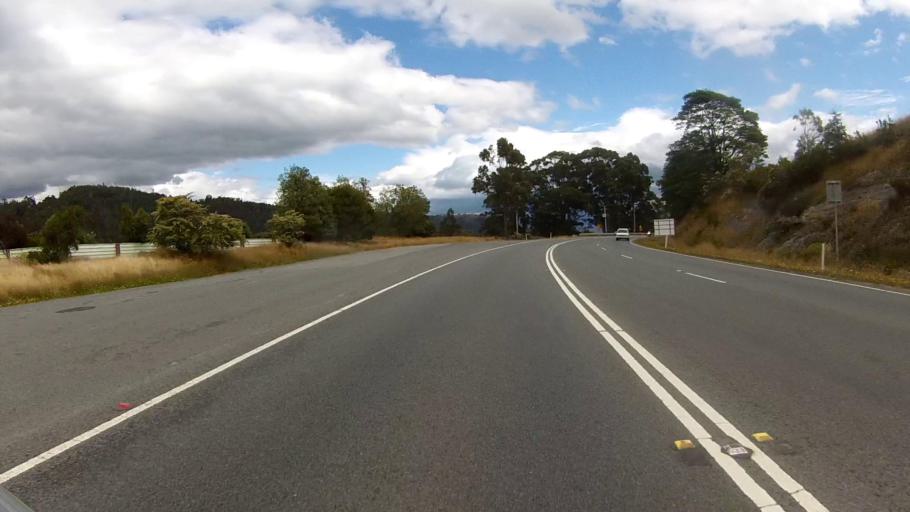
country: AU
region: Tasmania
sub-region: Kingborough
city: Margate
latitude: -42.9768
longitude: 147.1551
